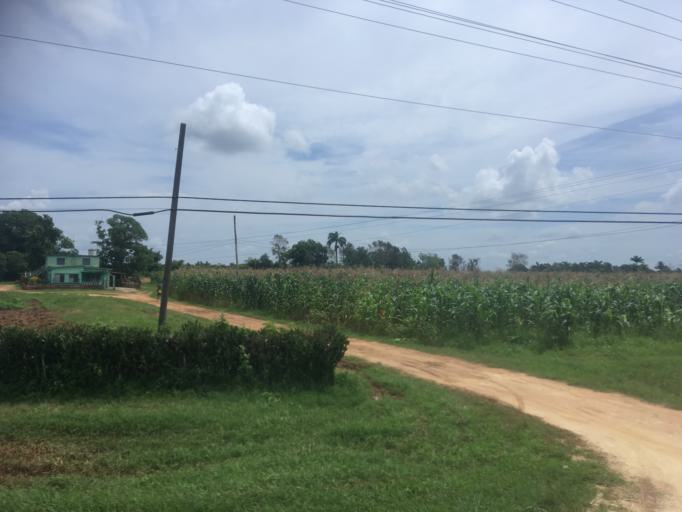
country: CU
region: Matanzas
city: Perico
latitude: 22.7772
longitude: -81.0344
